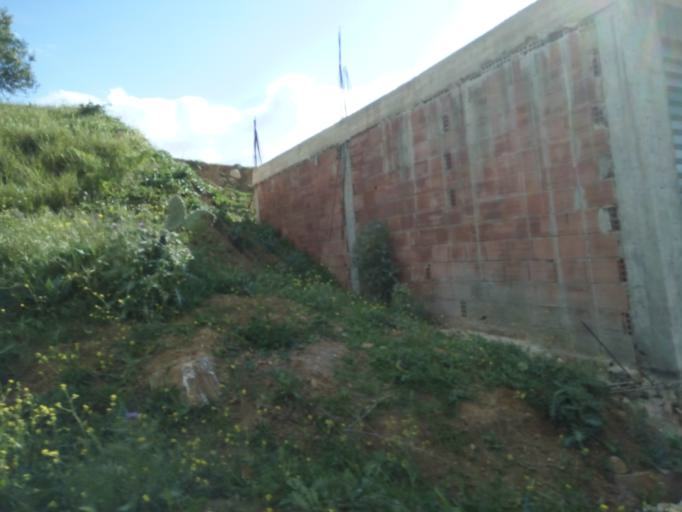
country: DZ
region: Tipaza
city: El Affroun
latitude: 36.3726
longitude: 2.4995
